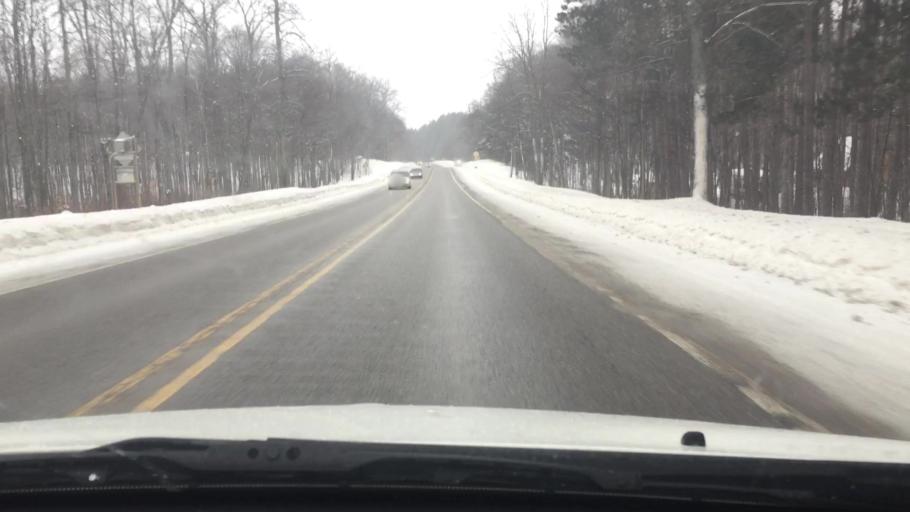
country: US
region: Michigan
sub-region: Otsego County
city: Gaylord
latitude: 45.0604
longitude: -84.7956
